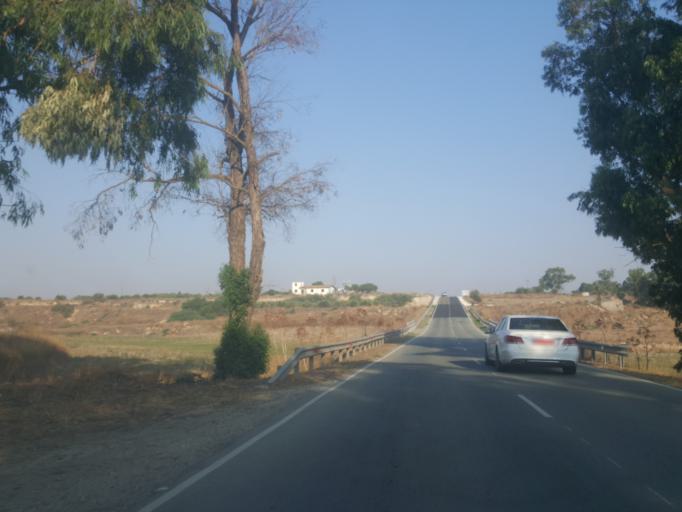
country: CY
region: Ammochostos
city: Avgorou
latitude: 35.0711
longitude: 33.8244
